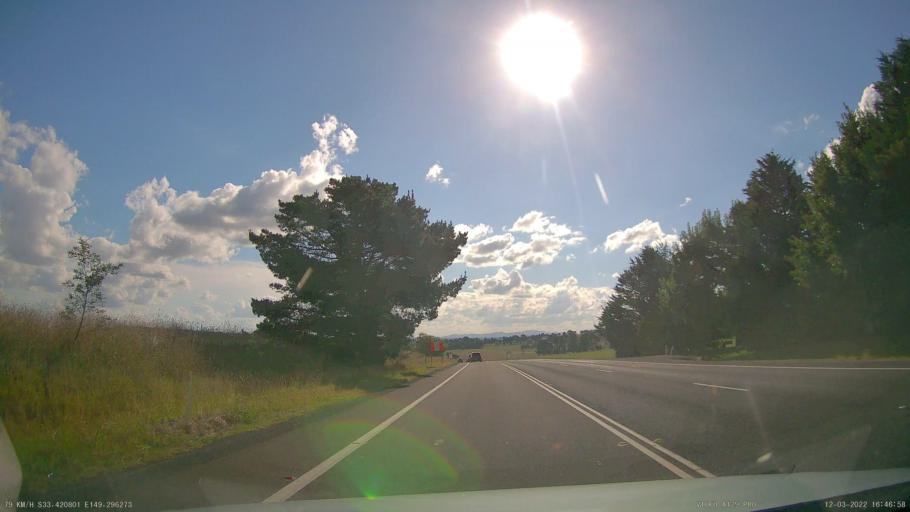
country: AU
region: New South Wales
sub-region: Blayney
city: Millthorpe
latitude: -33.4205
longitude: 149.2962
